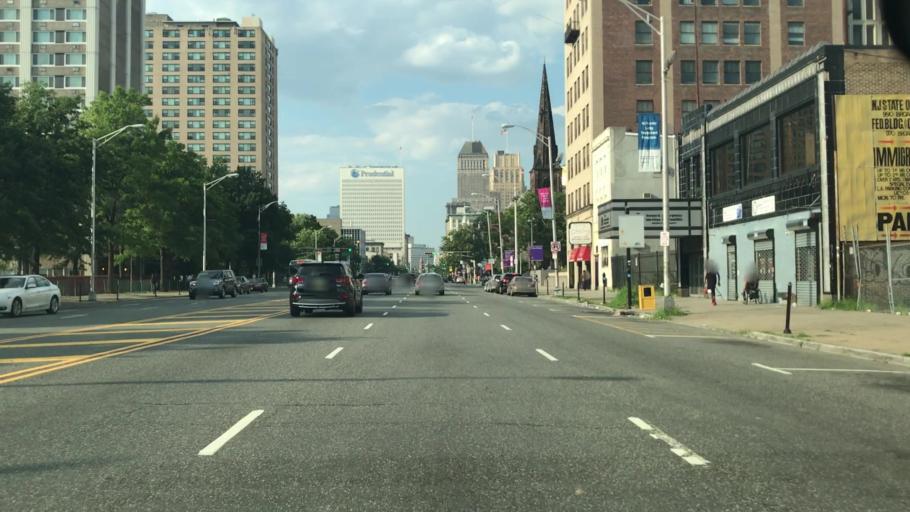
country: US
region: New Jersey
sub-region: Essex County
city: Newark
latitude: 40.7295
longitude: -74.1756
